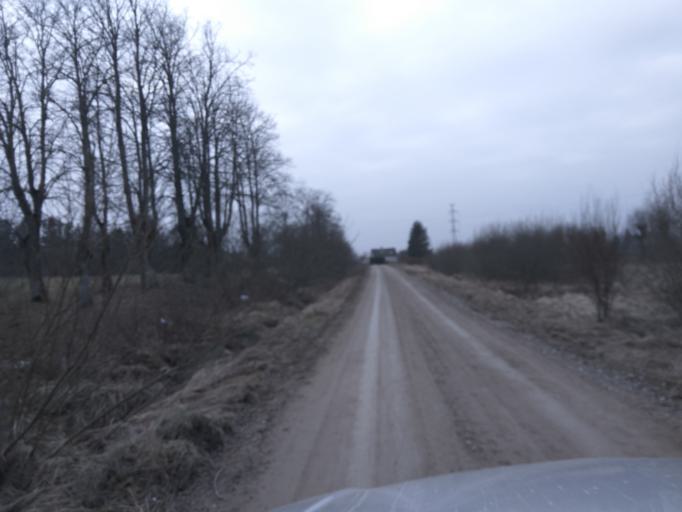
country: LV
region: Durbe
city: Liegi
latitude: 56.6729
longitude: 21.3561
